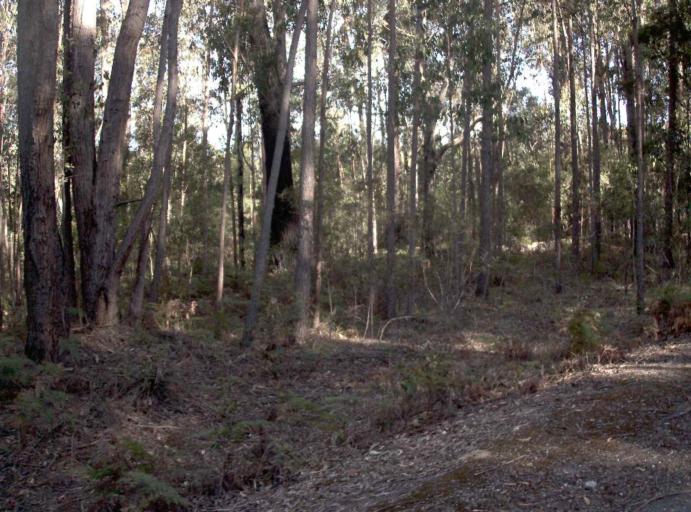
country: AU
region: Victoria
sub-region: East Gippsland
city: Lakes Entrance
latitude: -37.6310
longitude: 148.4876
